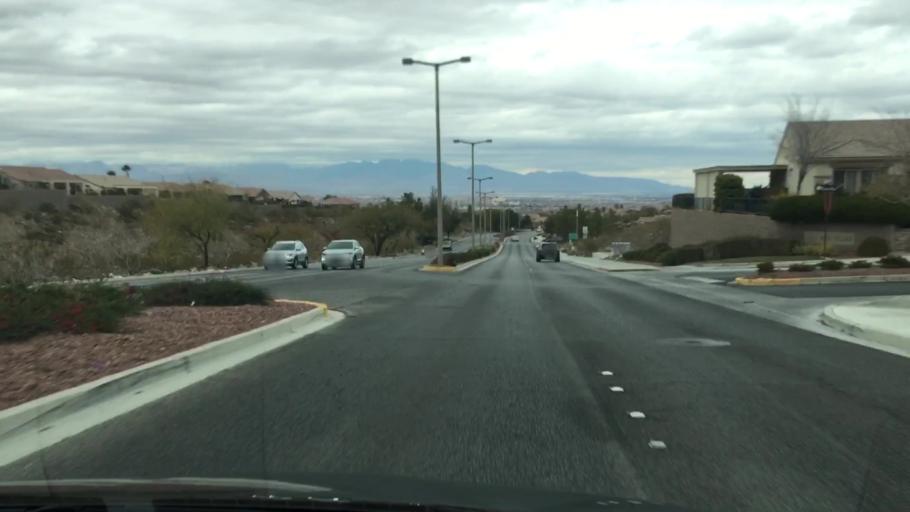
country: US
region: Nevada
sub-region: Clark County
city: Whitney
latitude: 35.9577
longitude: -115.1165
